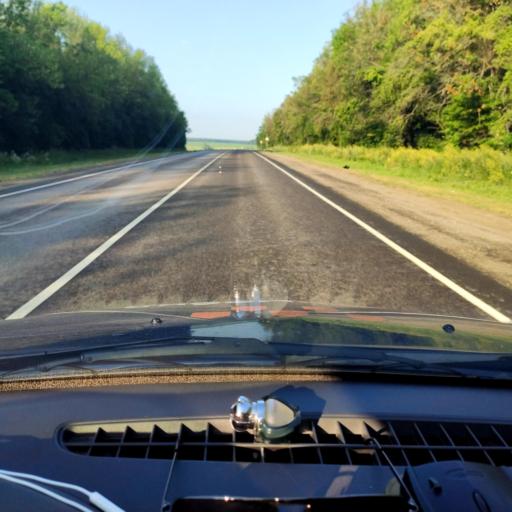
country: RU
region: Lipetsk
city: Izmalkovo
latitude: 52.4671
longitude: 38.0177
